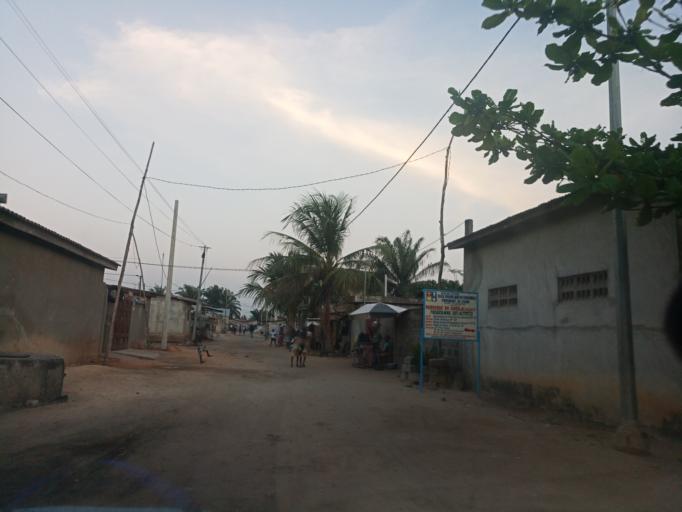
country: BJ
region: Atlantique
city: Hevie
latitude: 6.3928
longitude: 2.2888
